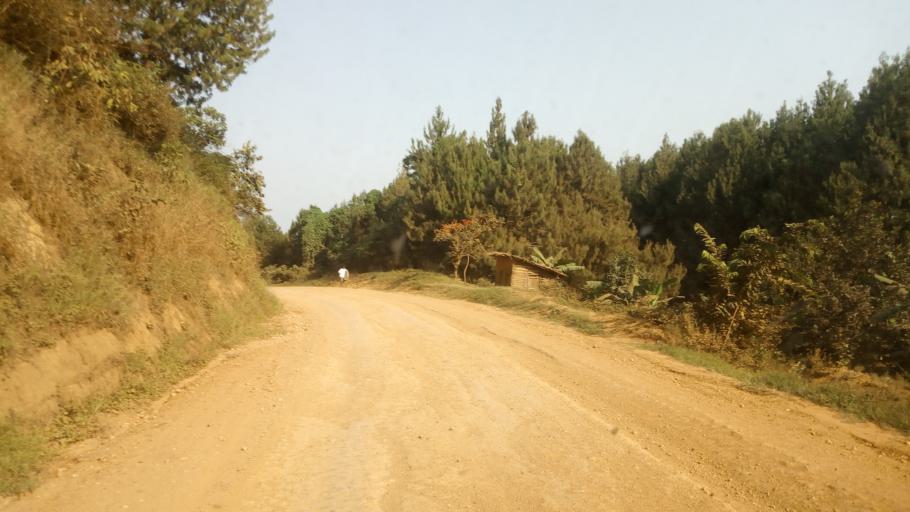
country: UG
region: Western Region
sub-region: Kanungu District
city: Ntungamo
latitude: -0.8272
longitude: 29.7053
